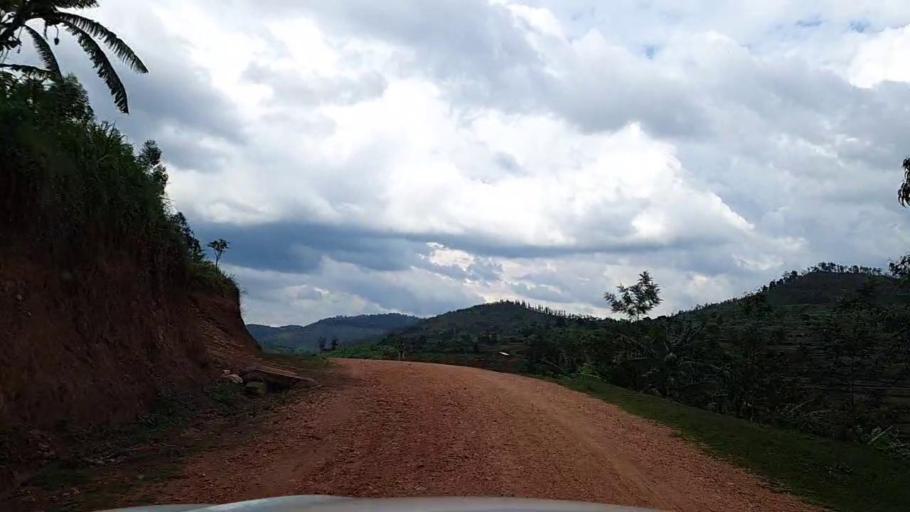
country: RW
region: Southern Province
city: Nyanza
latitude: -2.4099
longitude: 29.6757
